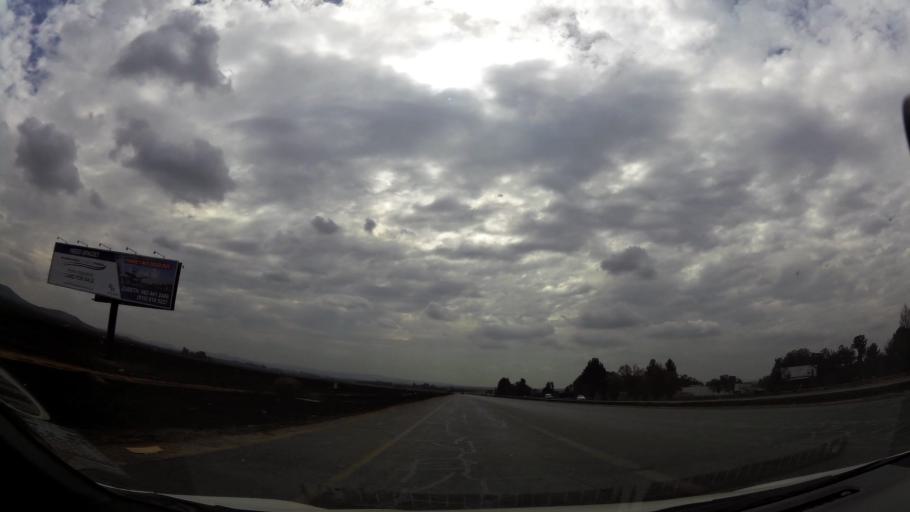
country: ZA
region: Gauteng
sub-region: Sedibeng District Municipality
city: Meyerton
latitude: -26.4120
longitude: 28.0780
